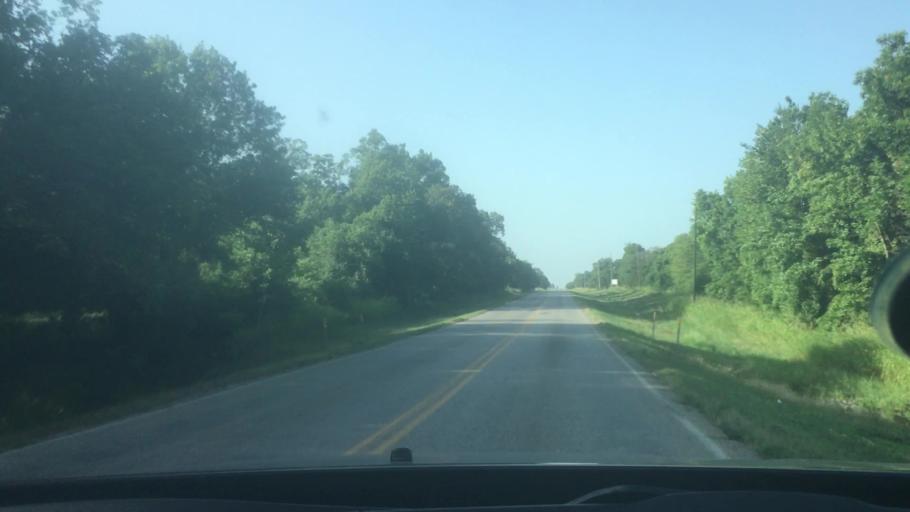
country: US
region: Oklahoma
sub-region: Johnston County
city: Tishomingo
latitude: 34.2982
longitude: -96.4248
